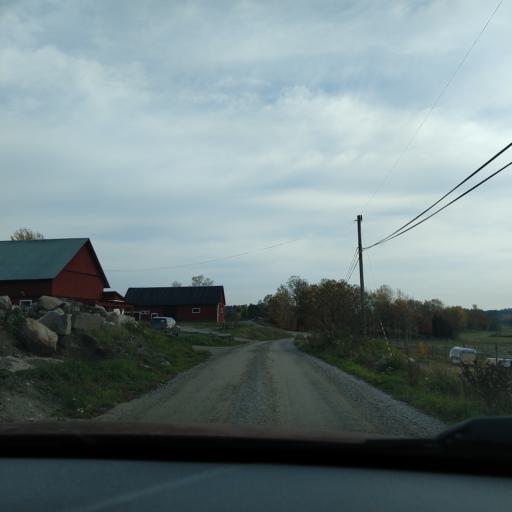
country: SE
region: Stockholm
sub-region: Vallentuna Kommun
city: Vallentuna
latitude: 59.5286
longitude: 18.0102
